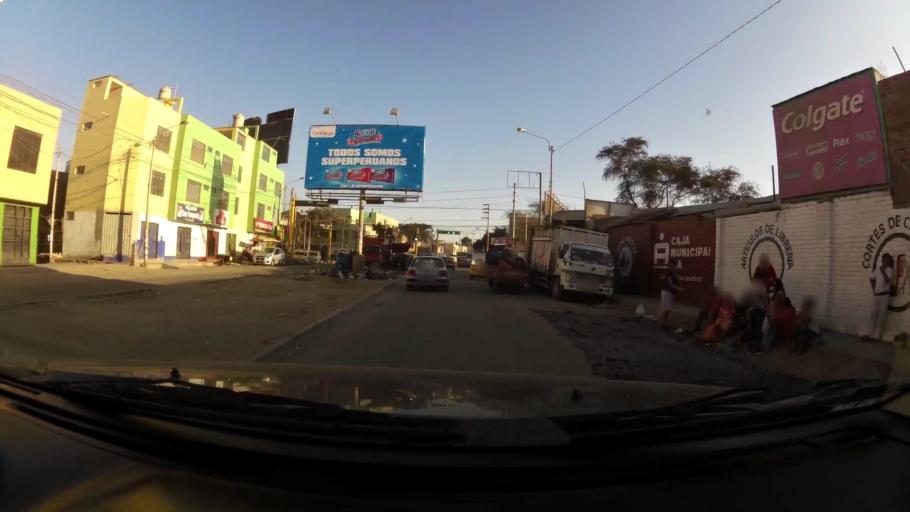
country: PE
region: Ica
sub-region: Provincia de Ica
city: Ica
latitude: -14.0601
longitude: -75.7348
